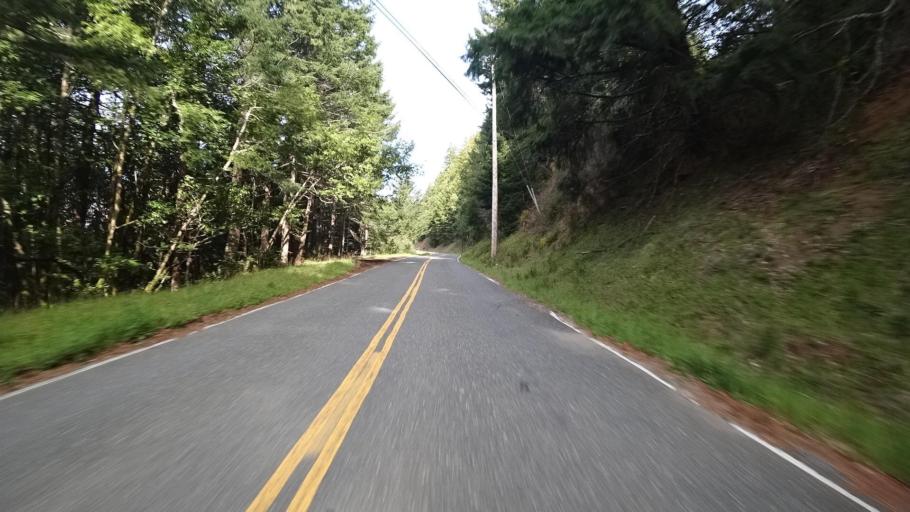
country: US
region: California
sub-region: Humboldt County
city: Bayside
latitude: 40.7467
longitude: -123.9661
